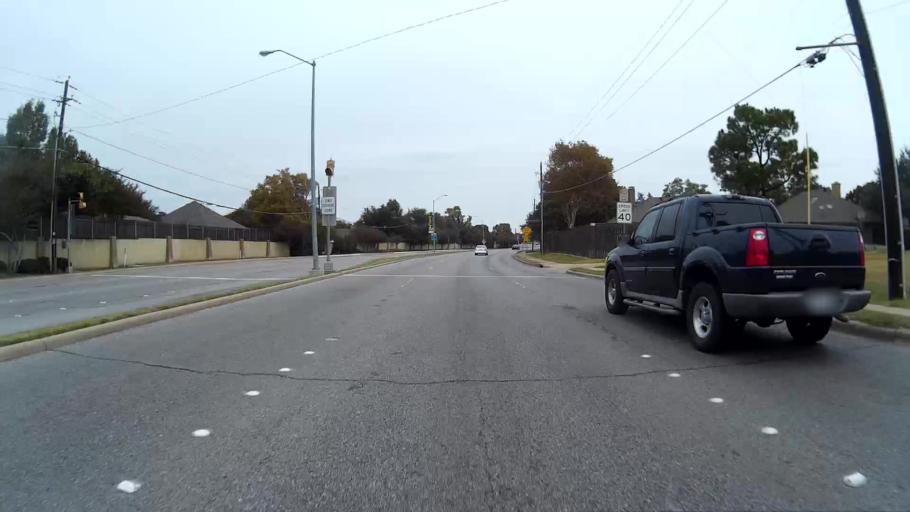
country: US
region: Texas
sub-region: Dallas County
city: Richardson
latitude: 32.9742
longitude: -96.7688
